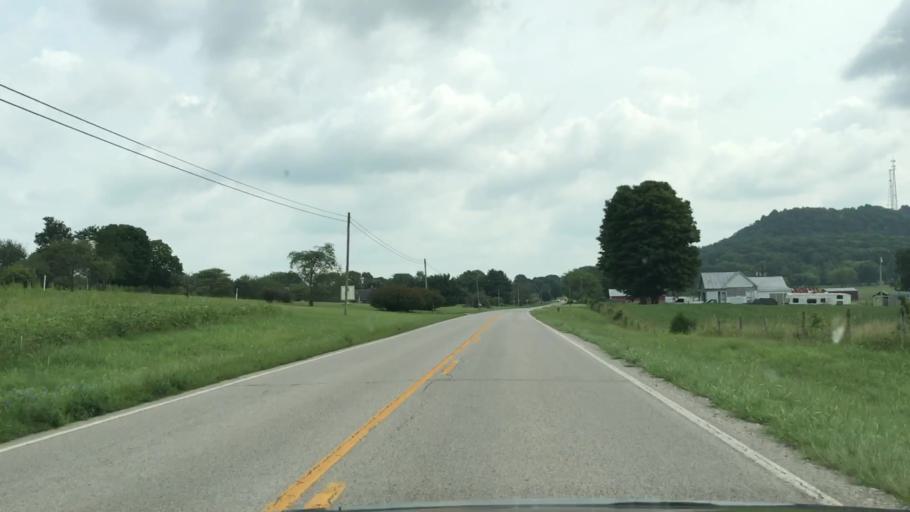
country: US
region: Kentucky
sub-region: Barren County
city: Cave City
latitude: 37.1096
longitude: -85.9948
